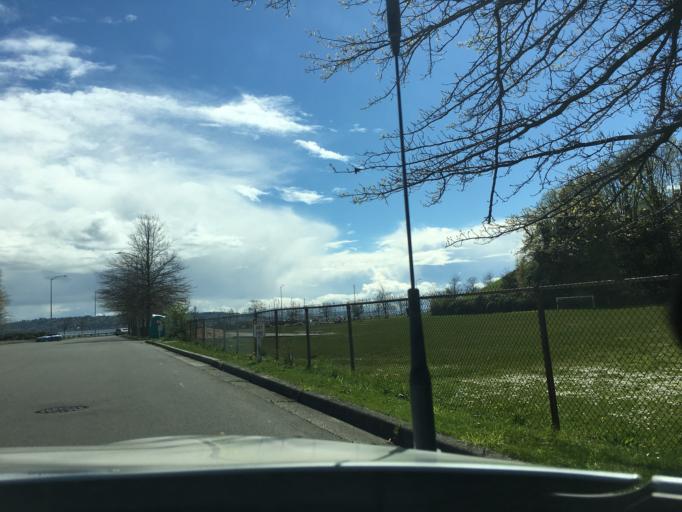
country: US
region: Washington
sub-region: King County
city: Seattle
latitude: 47.6329
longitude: -122.3870
